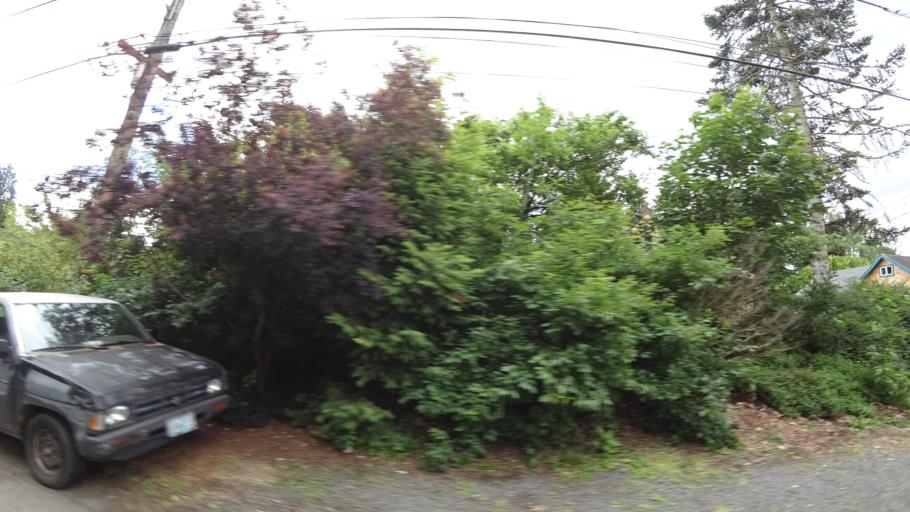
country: US
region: Oregon
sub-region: Multnomah County
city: Portland
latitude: 45.5600
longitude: -122.6174
